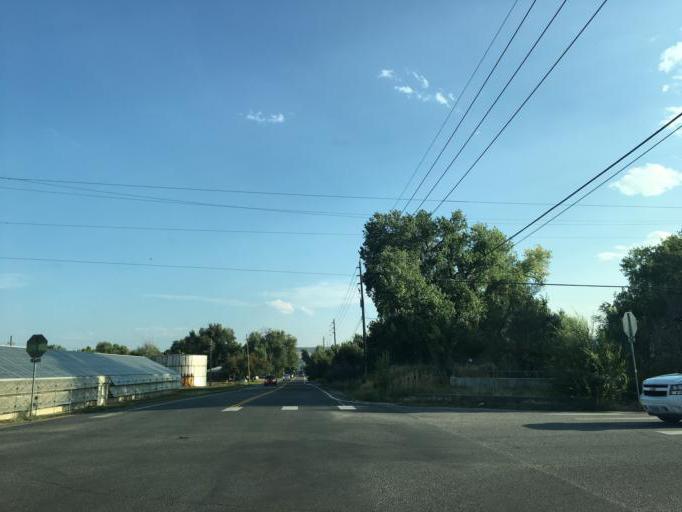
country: US
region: Colorado
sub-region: Jefferson County
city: Applewood
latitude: 39.7908
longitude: -105.1653
